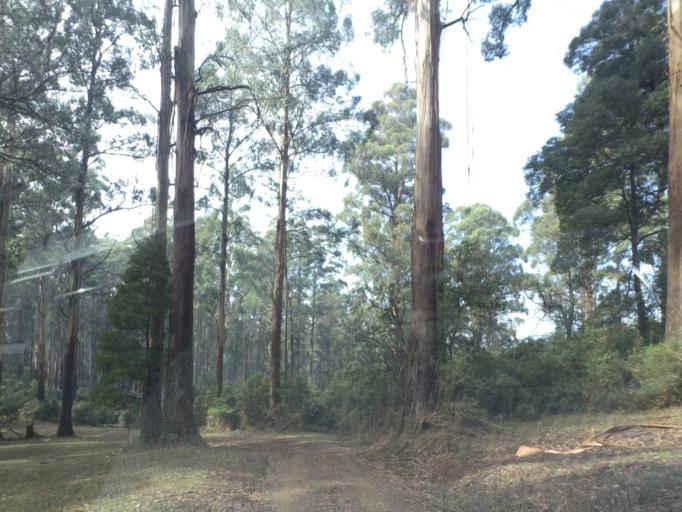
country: AU
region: Victoria
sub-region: Yarra Ranges
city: Healesville
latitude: -37.5721
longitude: 145.6157
